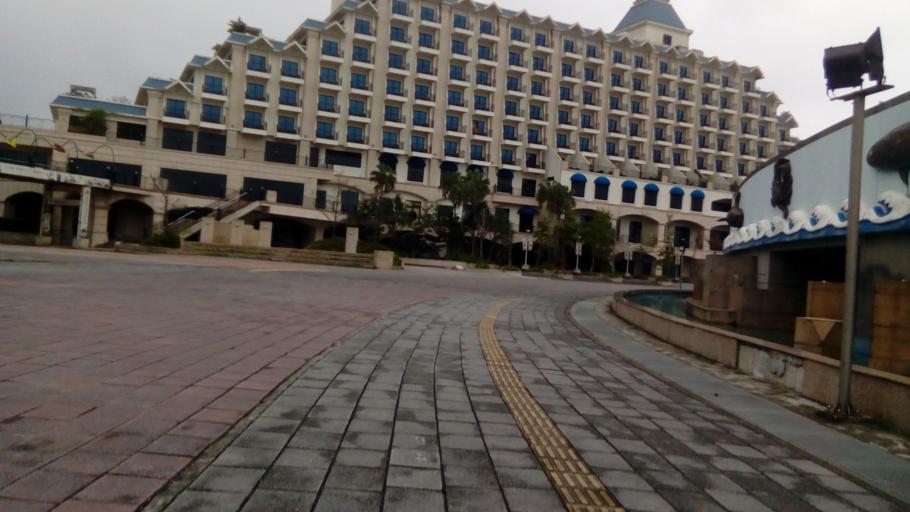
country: TW
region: Taipei
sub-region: Taipei
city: Banqiao
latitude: 25.1819
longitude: 121.4140
